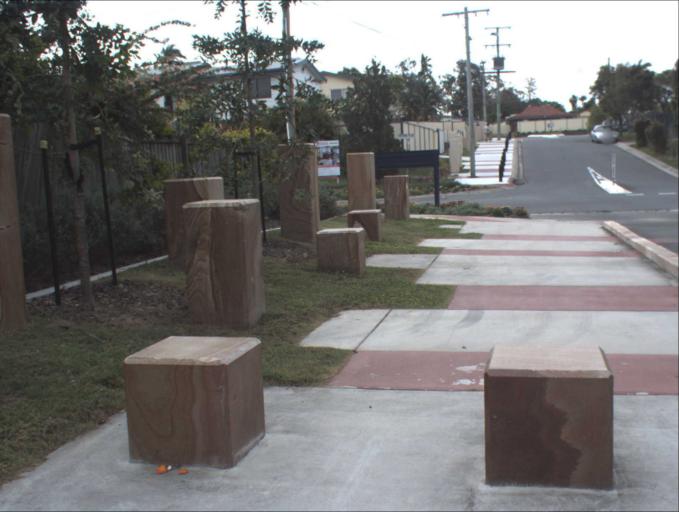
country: AU
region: Queensland
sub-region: Logan
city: Logan Reserve
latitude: -27.6898
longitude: 153.0925
